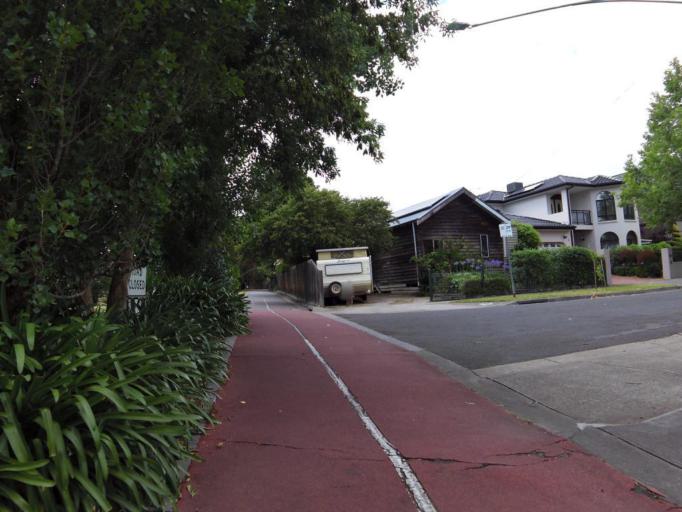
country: AU
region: Victoria
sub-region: Boroondara
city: Kew East
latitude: -37.7999
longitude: 145.0511
